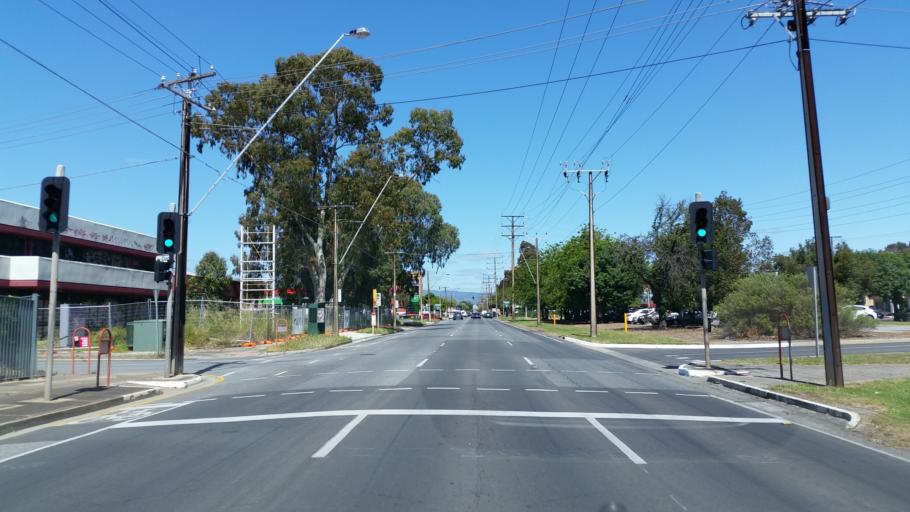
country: AU
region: South Australia
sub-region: Charles Sturt
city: Woodville West
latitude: -34.8788
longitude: 138.5326
